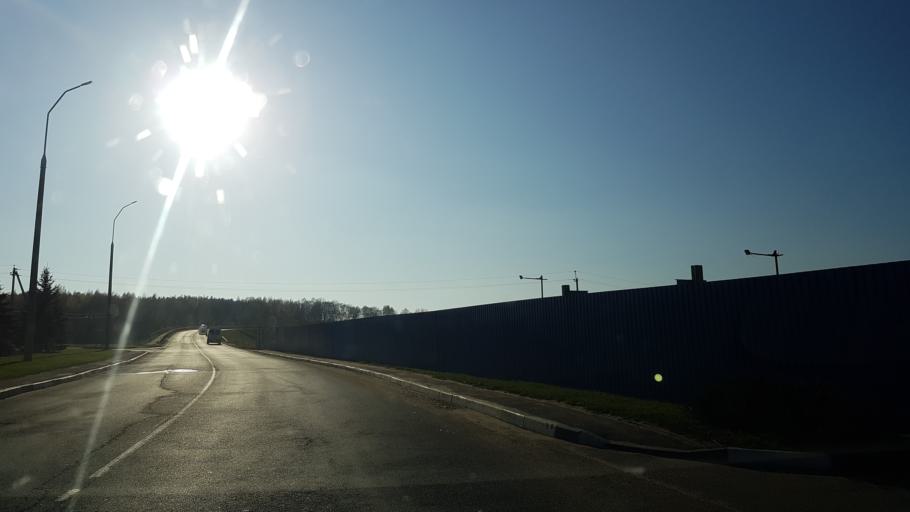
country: BY
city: Fanipol
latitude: 53.7365
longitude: 27.3083
